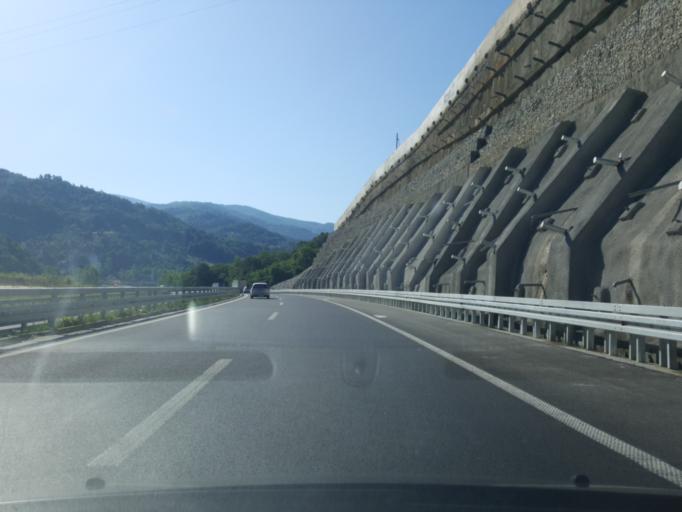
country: RS
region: Central Serbia
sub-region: Jablanicki Okrug
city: Vlasotince
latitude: 42.8657
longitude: 22.1085
